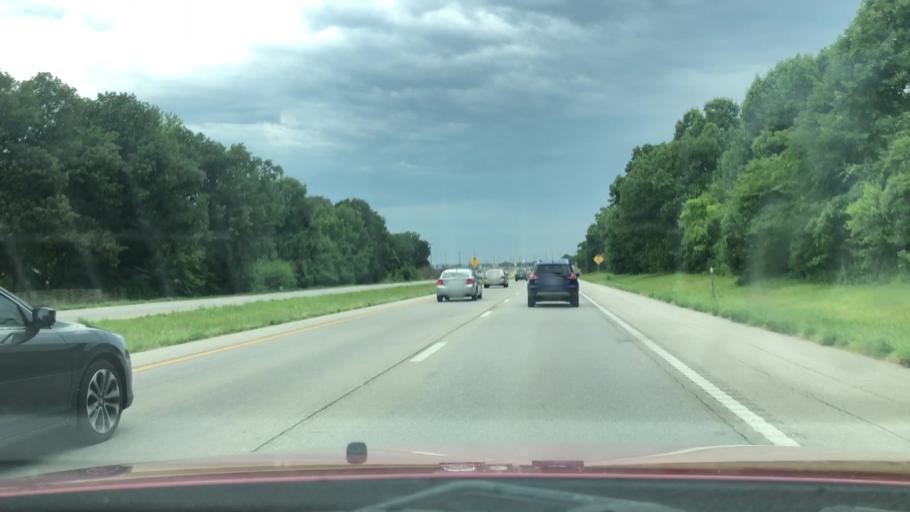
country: US
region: Missouri
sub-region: Greene County
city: Republic
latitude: 37.1384
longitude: -93.4463
